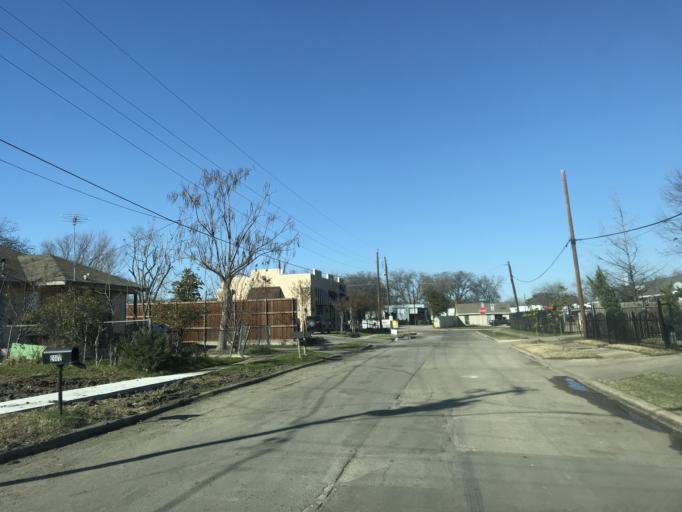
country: US
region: Texas
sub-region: Dallas County
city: Cockrell Hill
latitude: 32.7765
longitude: -96.9086
